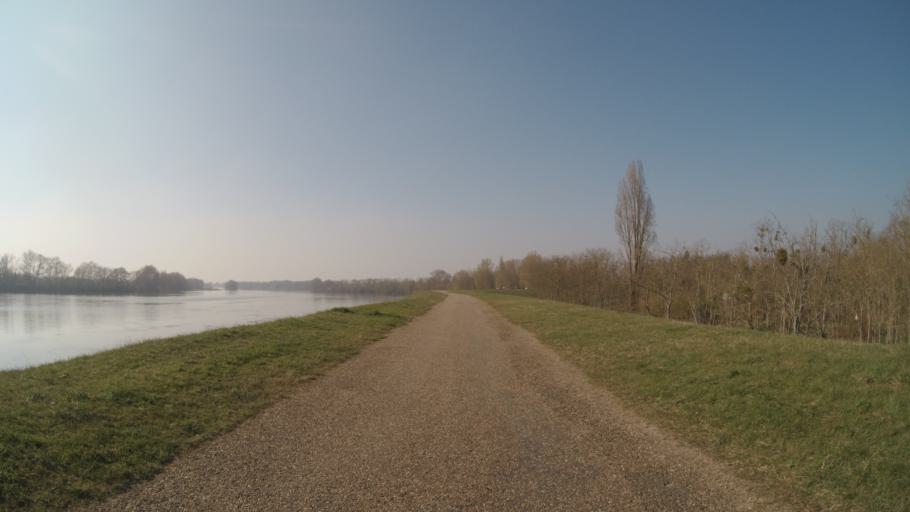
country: FR
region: Centre
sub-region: Departement du Loiret
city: Checy
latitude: 47.8827
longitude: 2.0316
